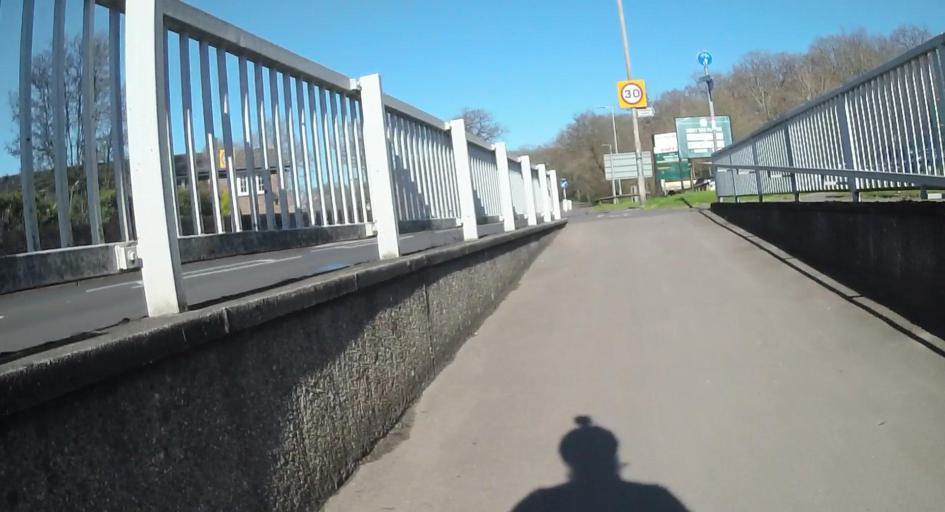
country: GB
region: England
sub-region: Bracknell Forest
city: Bracknell
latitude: 51.4140
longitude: -0.7311
